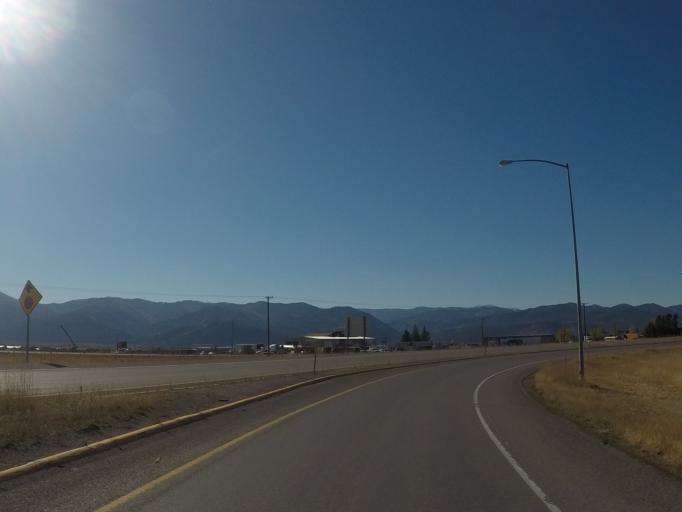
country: US
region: Montana
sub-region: Missoula County
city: Frenchtown
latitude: 46.9493
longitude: -114.1325
